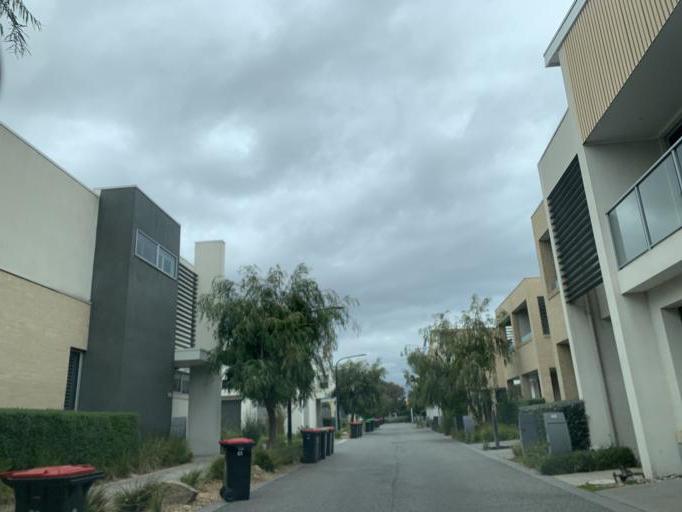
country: AU
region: Victoria
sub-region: Kingston
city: Mentone
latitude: -37.9753
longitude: 145.0706
